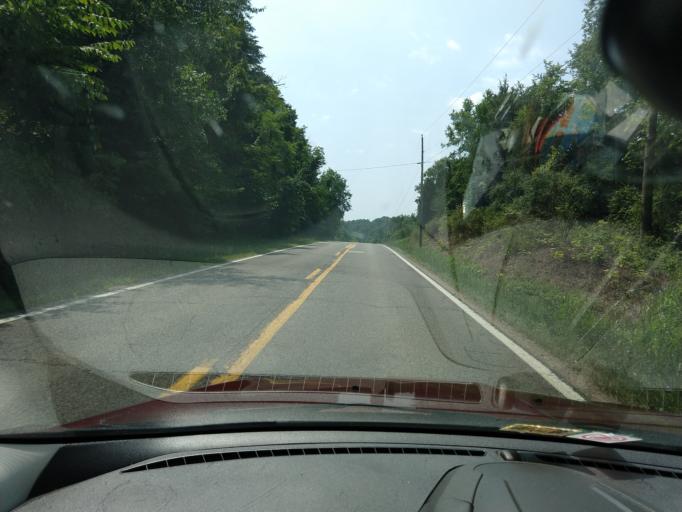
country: US
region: West Virginia
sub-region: Jackson County
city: Ripley
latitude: 38.8475
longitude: -81.7987
